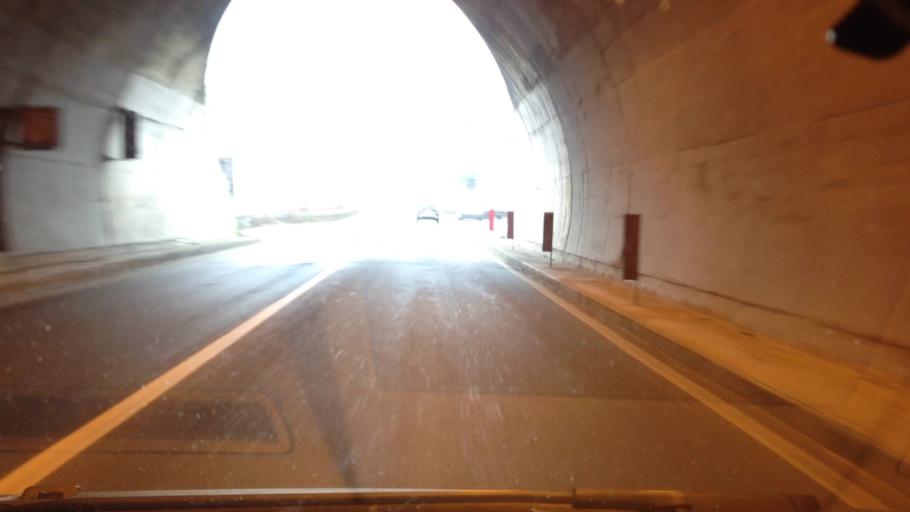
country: IT
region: Piedmont
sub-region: Provincia di Asti
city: Isola d'Asti
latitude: 44.8407
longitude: 8.1959
